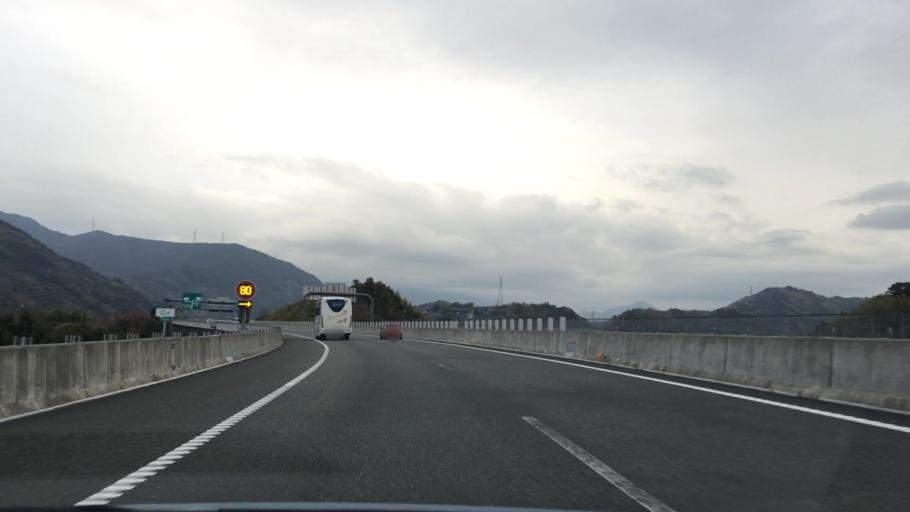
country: JP
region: Shizuoka
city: Shizuoka-shi
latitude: 35.0502
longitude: 138.4871
